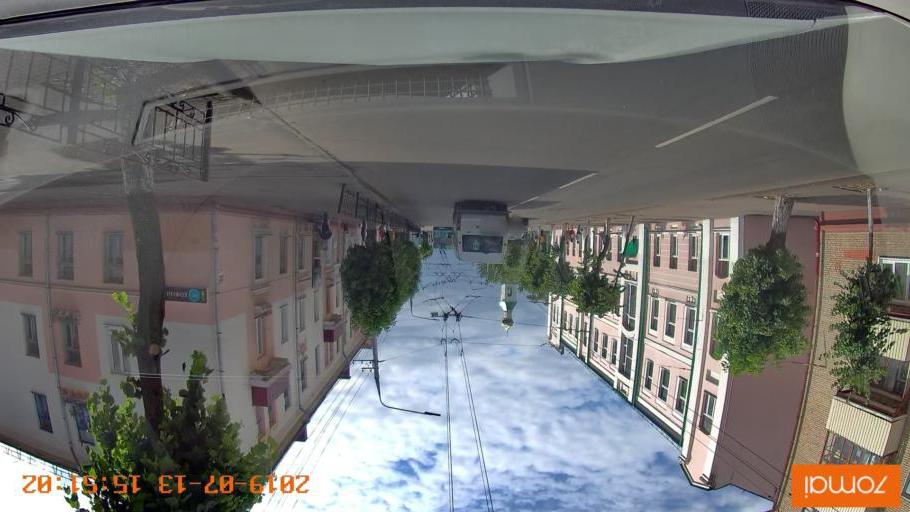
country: BY
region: Mogilev
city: Babruysk
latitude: 53.1405
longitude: 29.2244
